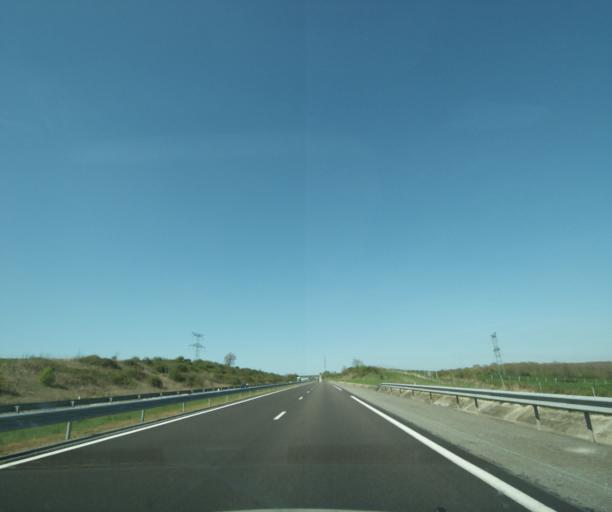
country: FR
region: Bourgogne
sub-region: Departement de la Nievre
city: Cosne-Cours-sur-Loire
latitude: 47.4537
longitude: 2.9480
